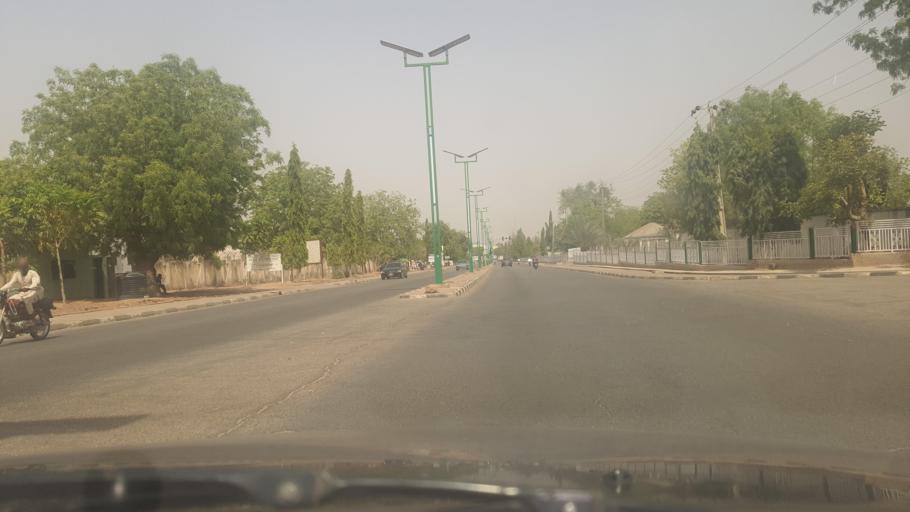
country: NG
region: Gombe
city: Gombe
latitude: 10.2822
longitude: 11.1567
